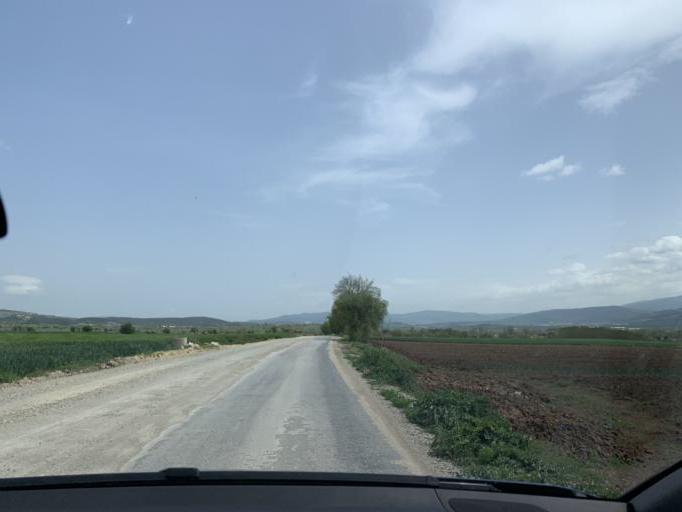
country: TR
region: Bolu
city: Bolu
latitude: 40.7563
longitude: 31.6784
